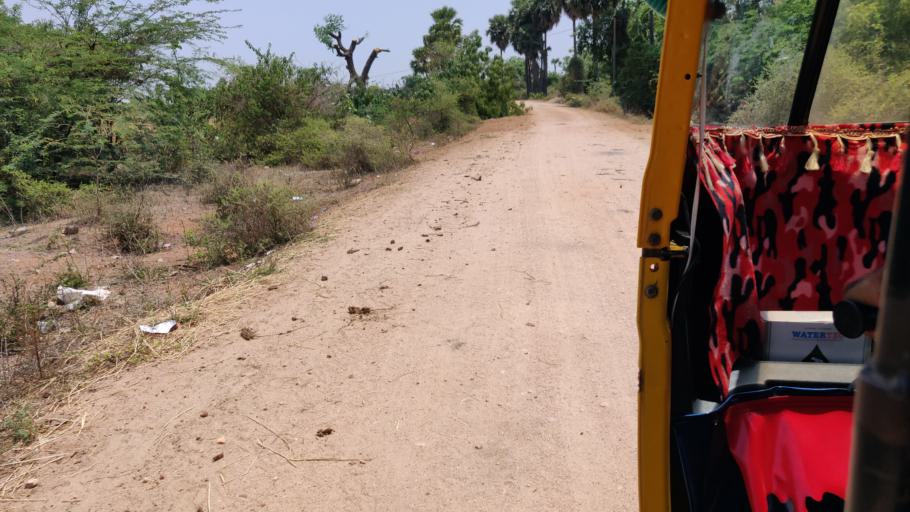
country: IN
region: Telangana
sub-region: Nalgonda
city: Mirialguda
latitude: 17.0117
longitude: 79.5459
